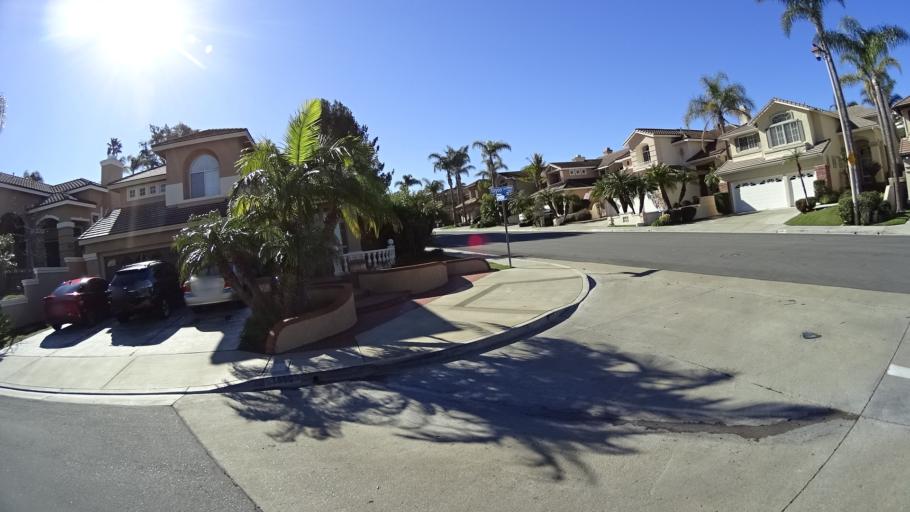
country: US
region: California
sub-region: Orange County
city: Villa Park
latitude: 33.8508
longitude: -117.7514
